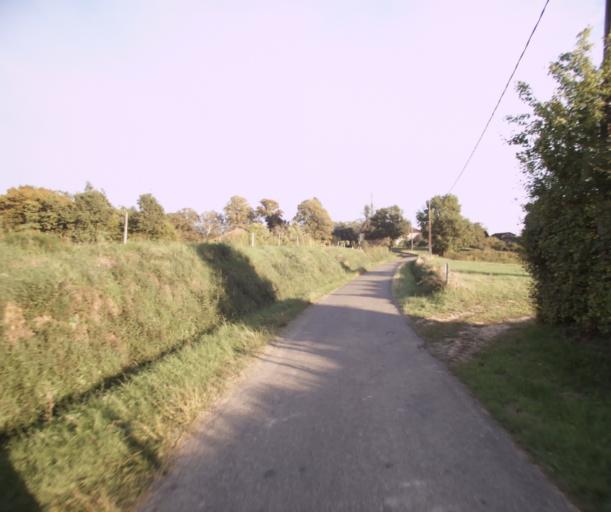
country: FR
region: Midi-Pyrenees
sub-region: Departement du Gers
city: Cazaubon
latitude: 43.8853
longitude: -0.0067
